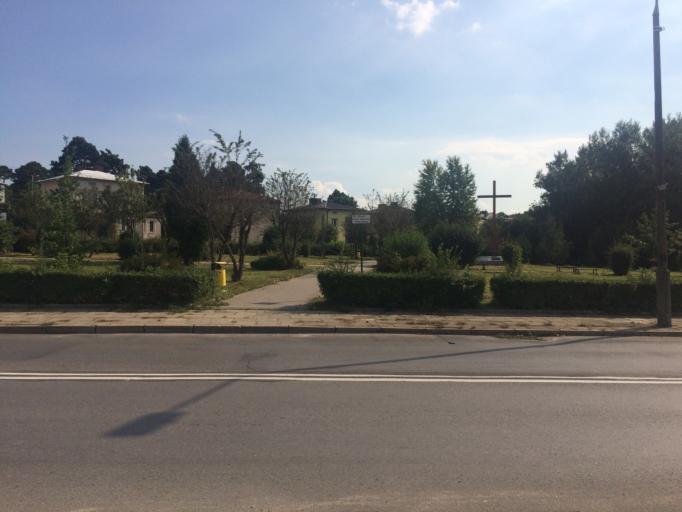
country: PL
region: Swietokrzyskie
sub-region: Powiat starachowicki
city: Starachowice
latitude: 51.0557
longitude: 21.0688
